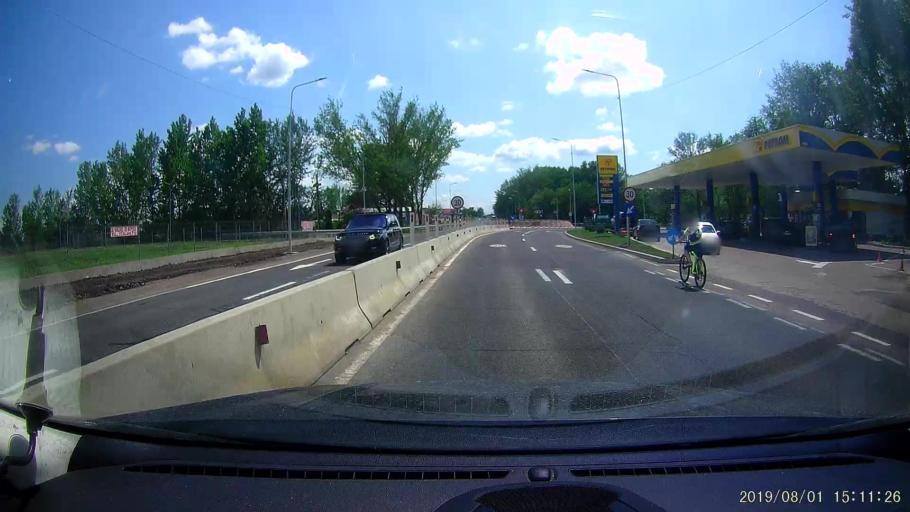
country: RO
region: Braila
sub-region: Comuna Chiscani
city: Chiscani
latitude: 45.2171
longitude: 27.9235
